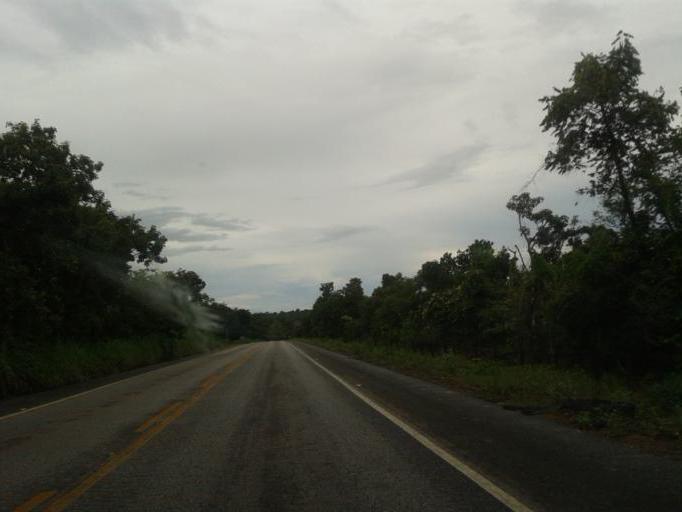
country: BR
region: Goias
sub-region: Mozarlandia
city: Mozarlandia
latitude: -14.8380
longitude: -50.5397
